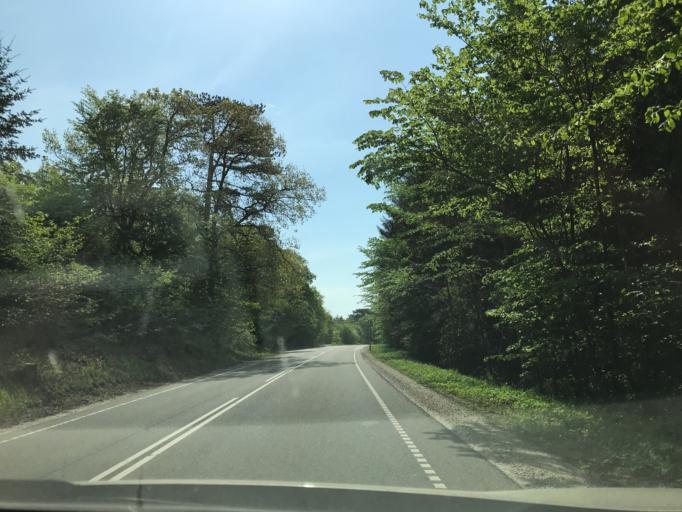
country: DK
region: South Denmark
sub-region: Middelfart Kommune
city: Ejby
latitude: 55.3922
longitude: 9.9116
